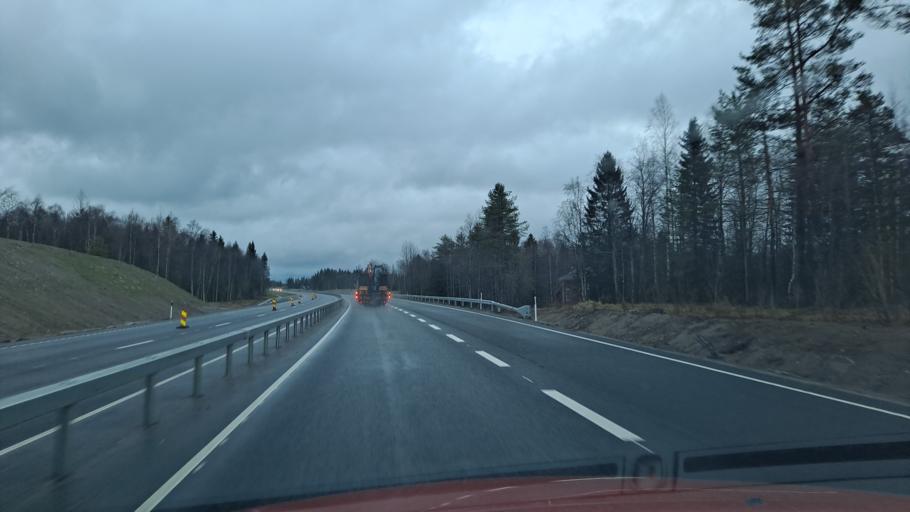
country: FI
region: Lapland
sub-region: Kemi-Tornio
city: Kemi
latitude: 65.6747
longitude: 24.7830
